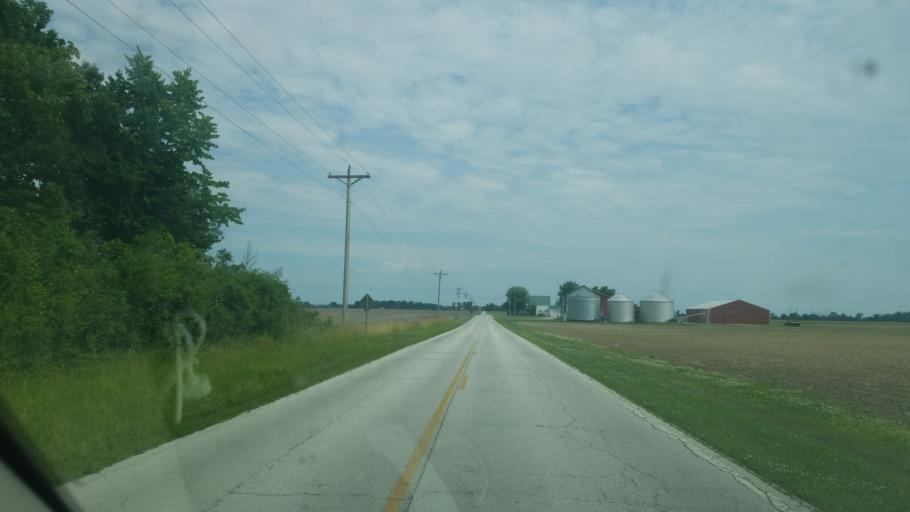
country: US
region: Ohio
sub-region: Seneca County
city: Fostoria
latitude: 41.1092
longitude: -83.4786
